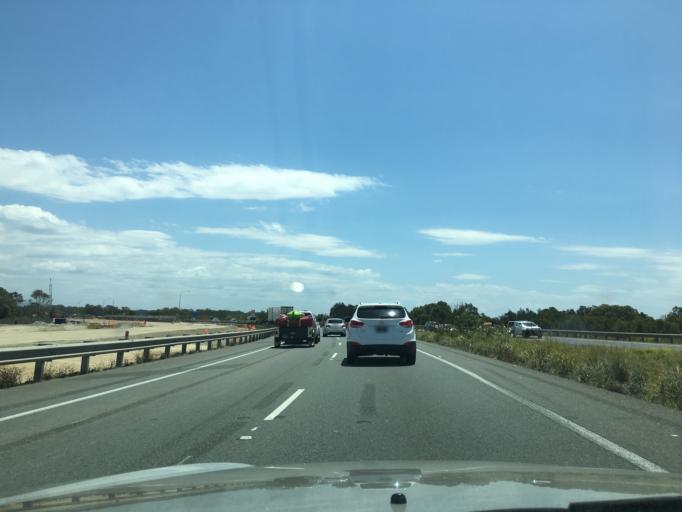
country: AU
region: Queensland
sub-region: Brisbane
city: Shorncliffe
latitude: -27.3581
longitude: 153.0917
